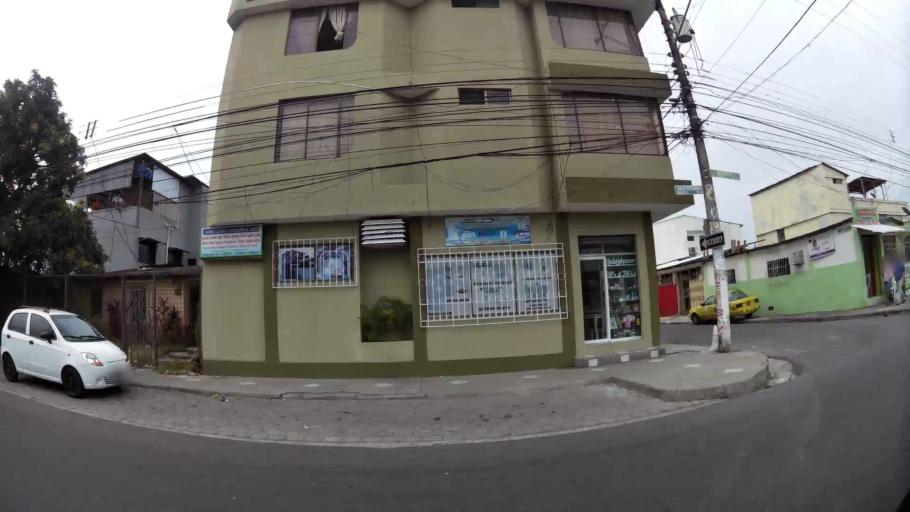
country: EC
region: Guayas
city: Eloy Alfaro
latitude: -2.1407
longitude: -79.9002
